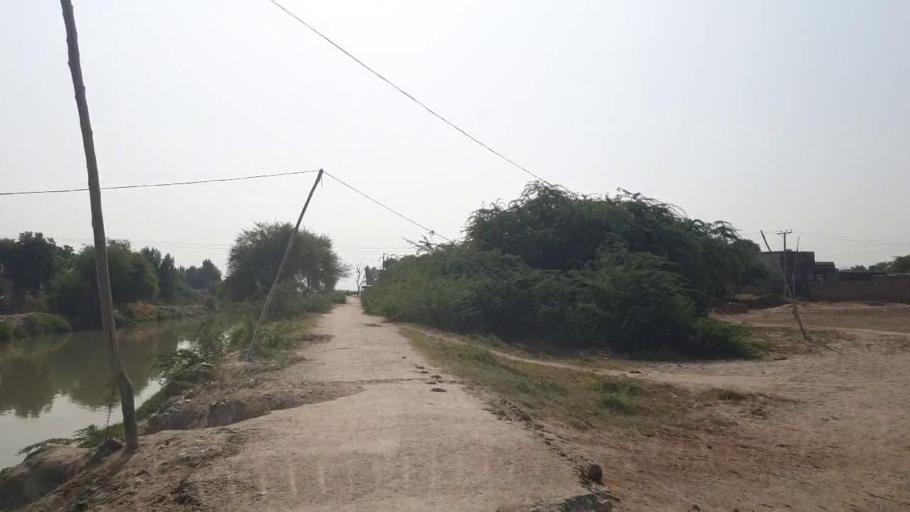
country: PK
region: Sindh
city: Badin
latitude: 24.6391
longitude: 68.8495
